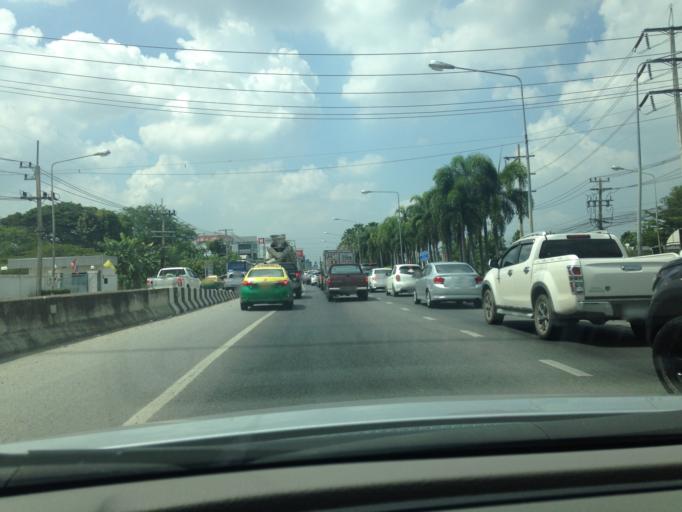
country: TH
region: Phra Nakhon Si Ayutthaya
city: Ban Bang Kadi Pathum Thani
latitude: 13.9847
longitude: 100.5891
